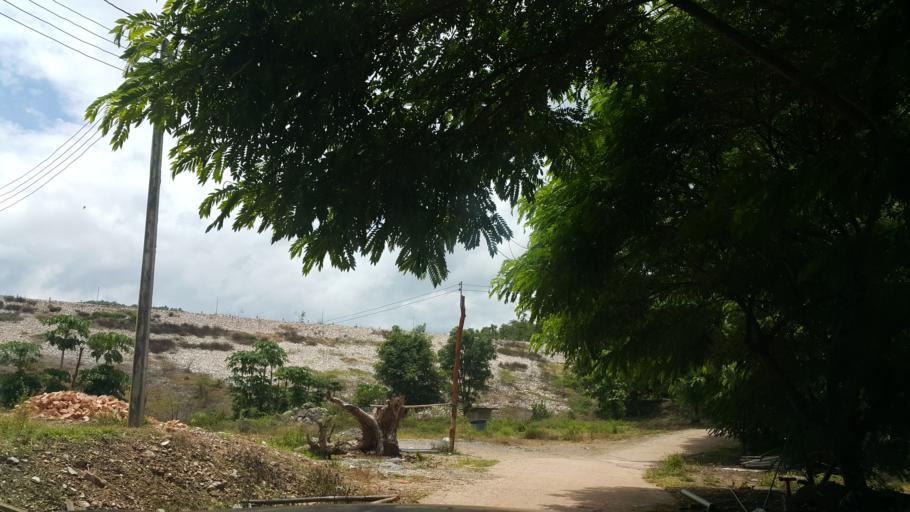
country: TH
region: Chiang Mai
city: Mae Taeng
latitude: 19.2247
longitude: 99.0100
